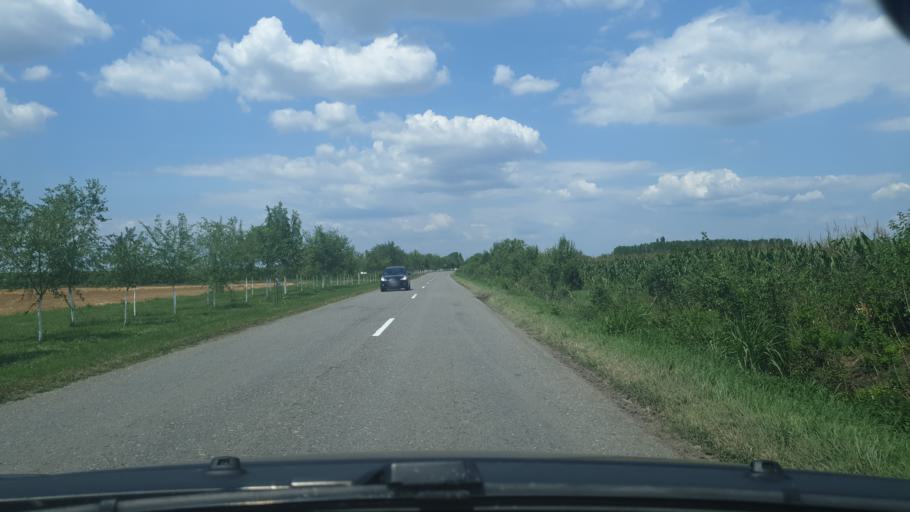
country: RS
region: Autonomna Pokrajina Vojvodina
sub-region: Sremski Okrug
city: Pecinci
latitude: 44.8559
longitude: 19.9607
